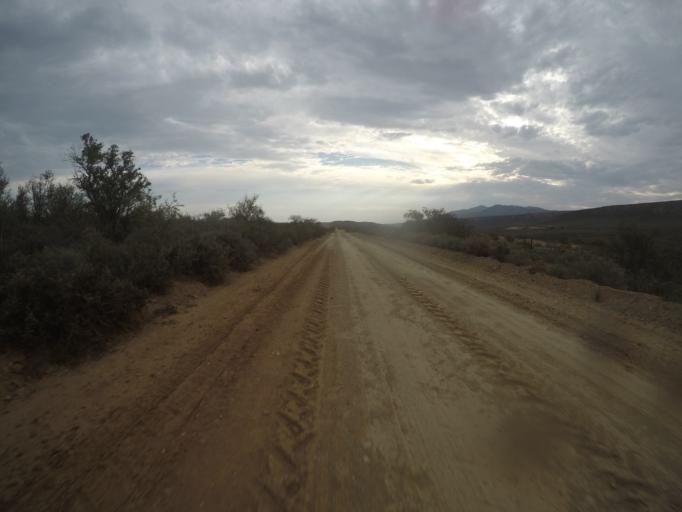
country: ZA
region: Eastern Cape
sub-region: Cacadu District Municipality
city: Willowmore
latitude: -33.4919
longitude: 23.5881
